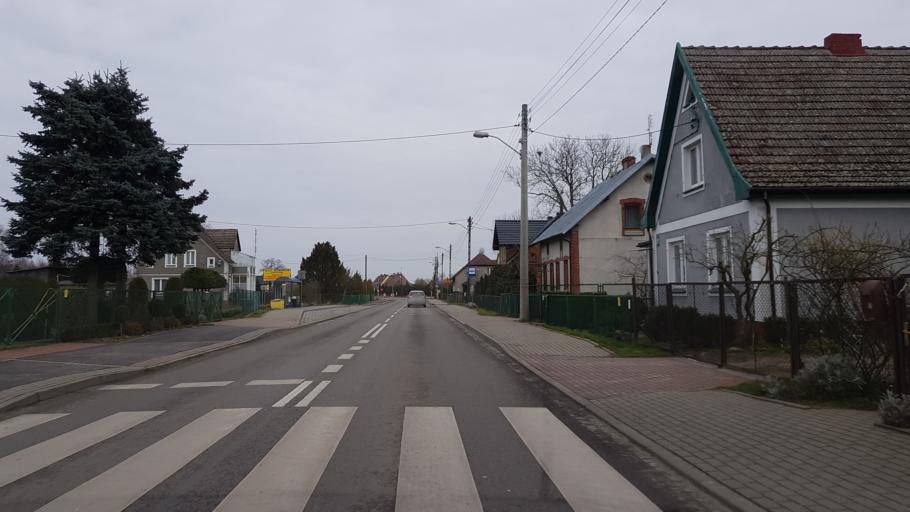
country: PL
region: West Pomeranian Voivodeship
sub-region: Powiat policki
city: Police
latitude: 53.6489
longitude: 14.5092
